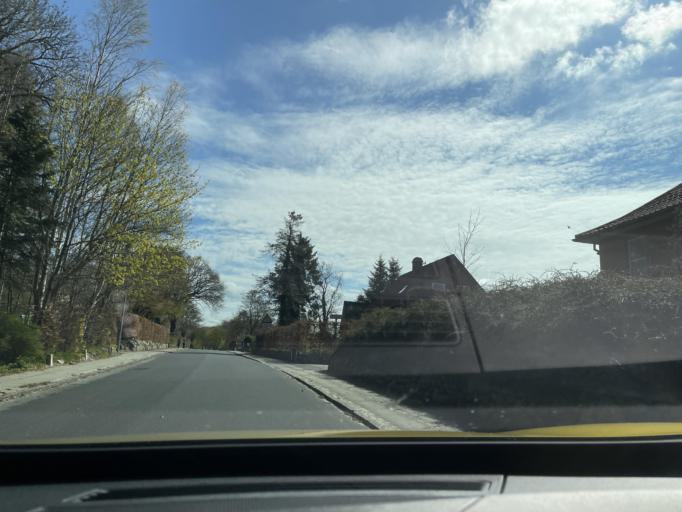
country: DK
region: Central Jutland
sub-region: Favrskov Kommune
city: Hadsten
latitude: 56.3245
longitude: 10.0570
